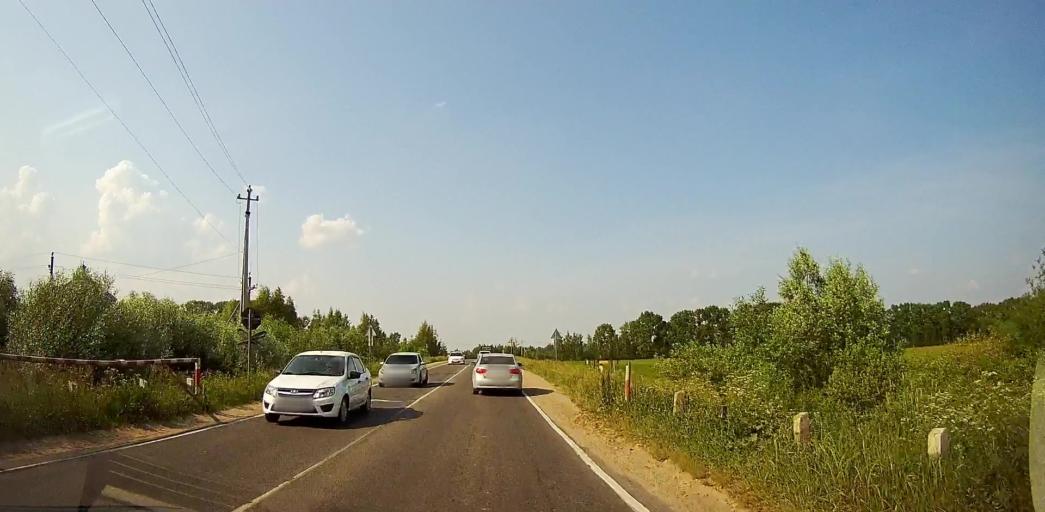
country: RU
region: Moskovskaya
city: Zhitnevo
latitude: 55.3185
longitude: 37.9001
